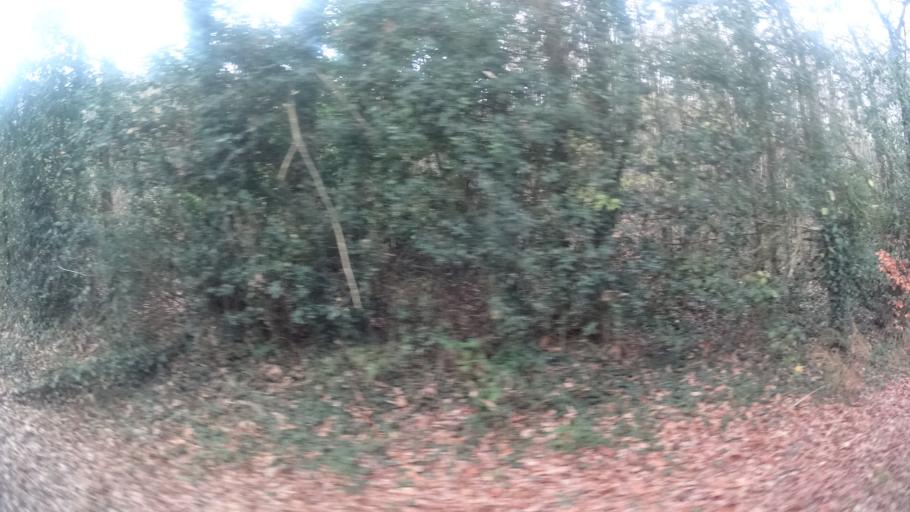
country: FR
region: Pays de la Loire
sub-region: Departement de la Loire-Atlantique
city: Avessac
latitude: 47.6523
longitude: -1.9826
